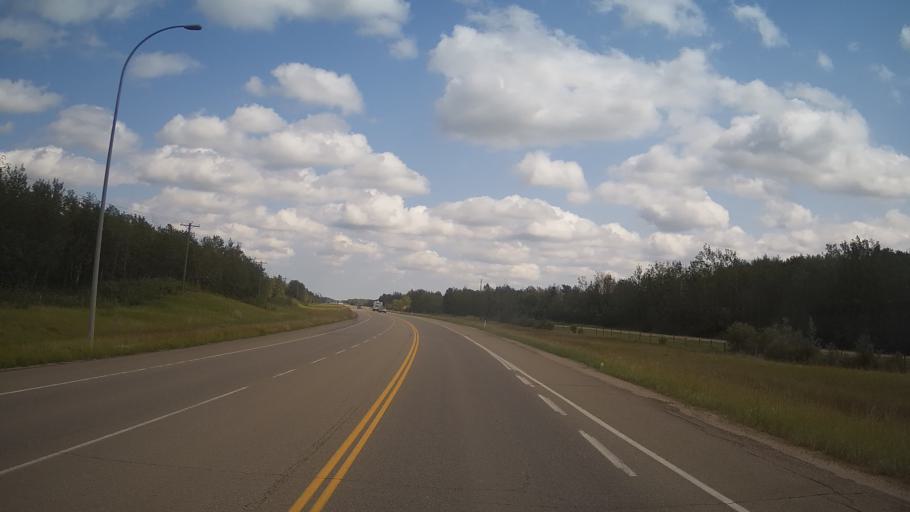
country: CA
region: Alberta
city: Sherwood Park
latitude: 53.3958
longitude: -113.0960
